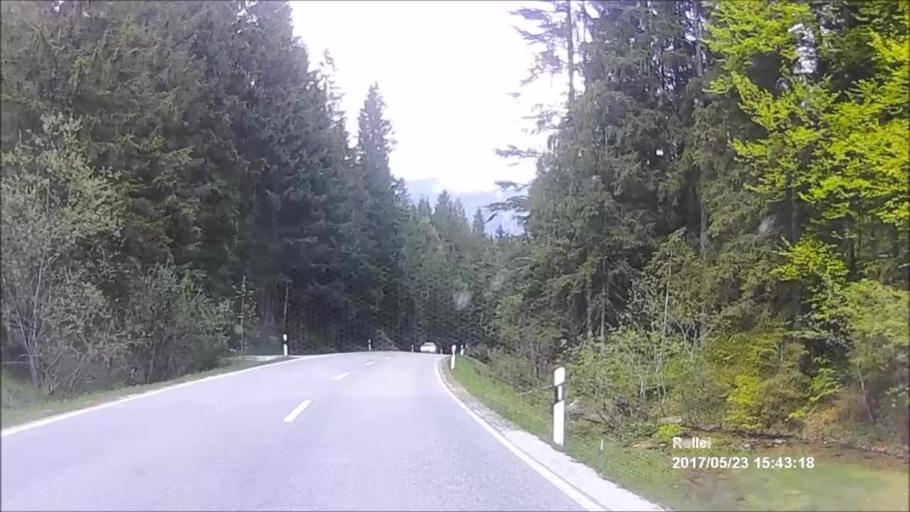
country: DE
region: Bavaria
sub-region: Upper Bavaria
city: Ramsau
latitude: 47.6427
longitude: 12.9173
